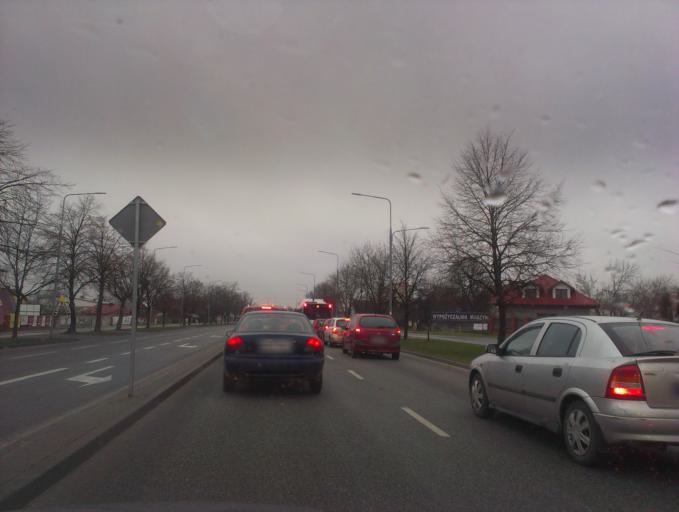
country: PL
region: Masovian Voivodeship
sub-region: Radom
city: Radom
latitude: 51.4249
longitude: 21.1509
